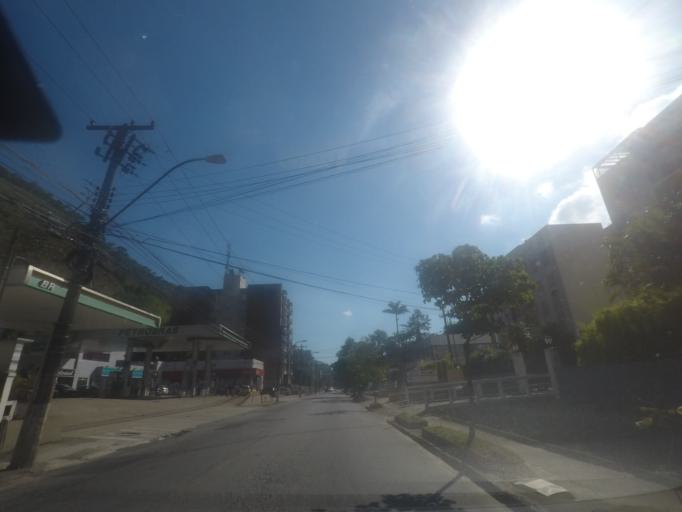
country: BR
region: Rio de Janeiro
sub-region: Petropolis
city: Petropolis
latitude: -22.5250
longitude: -43.1925
